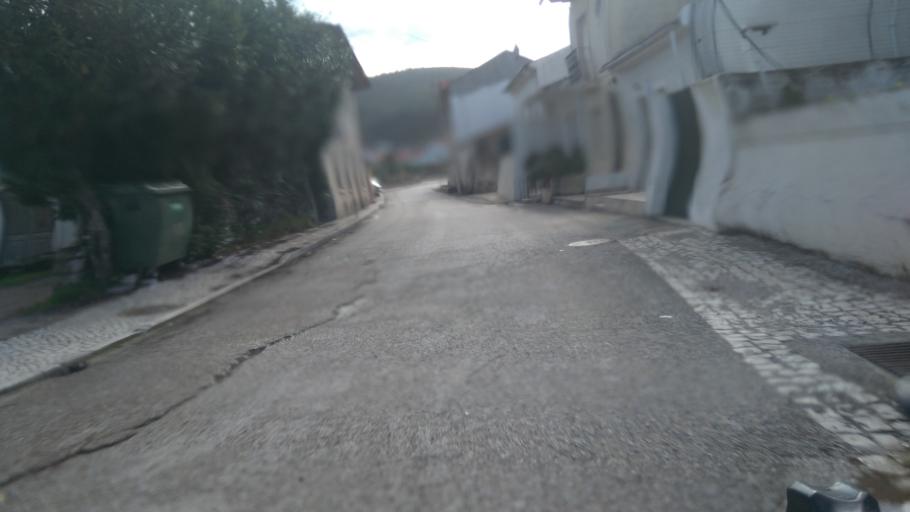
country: PT
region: Leiria
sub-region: Porto de Mos
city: Porto de Mos
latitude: 39.5877
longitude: -8.8205
